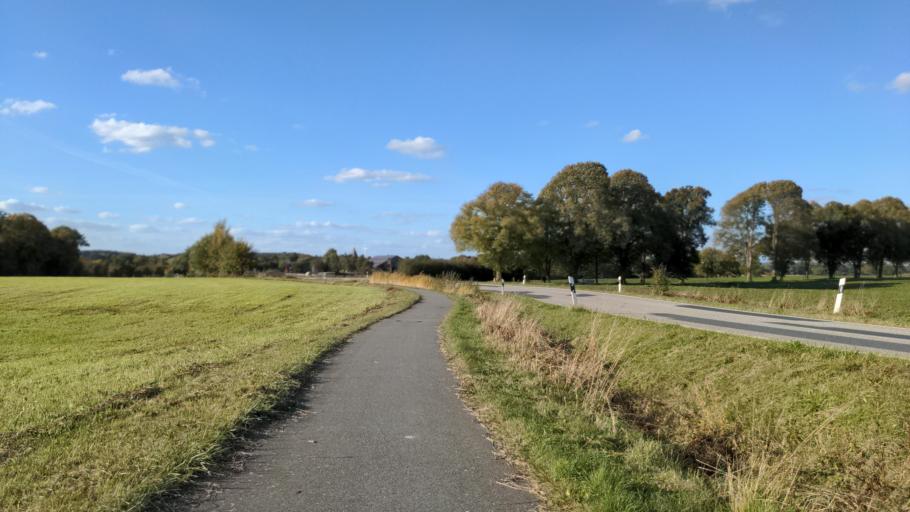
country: DE
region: Schleswig-Holstein
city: Zarpen
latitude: 53.8643
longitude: 10.5278
